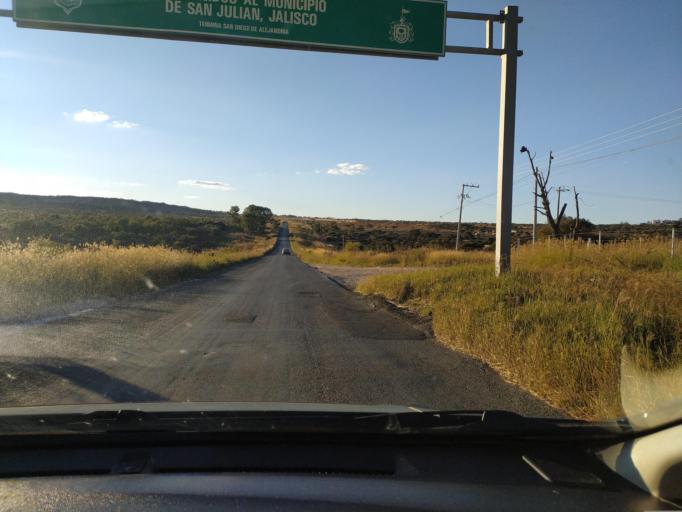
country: MX
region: Jalisco
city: San Julian
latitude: 21.0044
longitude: -102.1132
